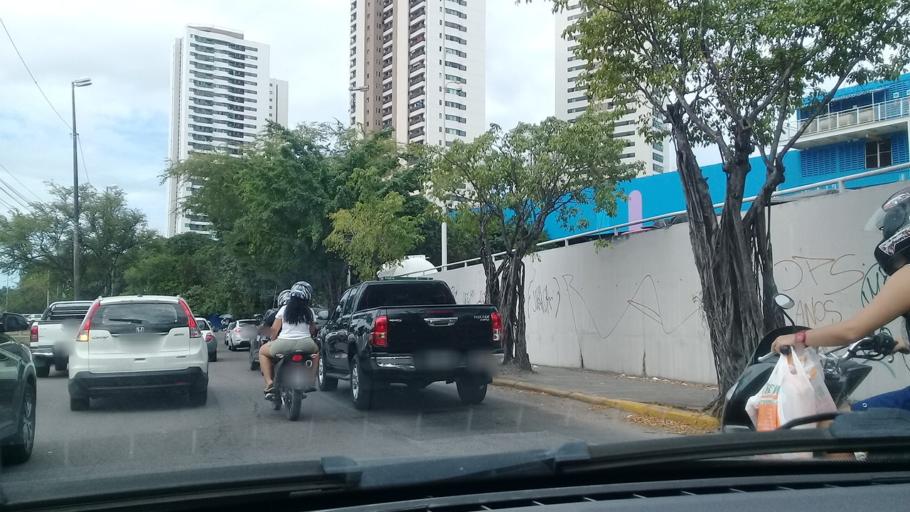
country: BR
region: Pernambuco
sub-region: Recife
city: Recife
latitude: -8.1153
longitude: -34.9034
